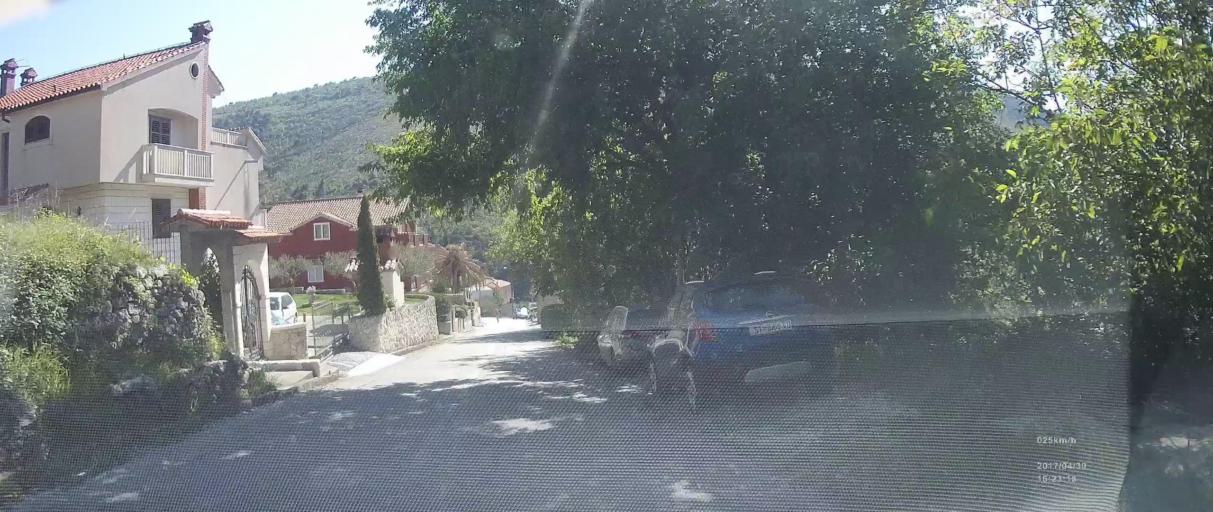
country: HR
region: Splitsko-Dalmatinska
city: Srinjine
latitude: 43.5107
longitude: 16.5927
